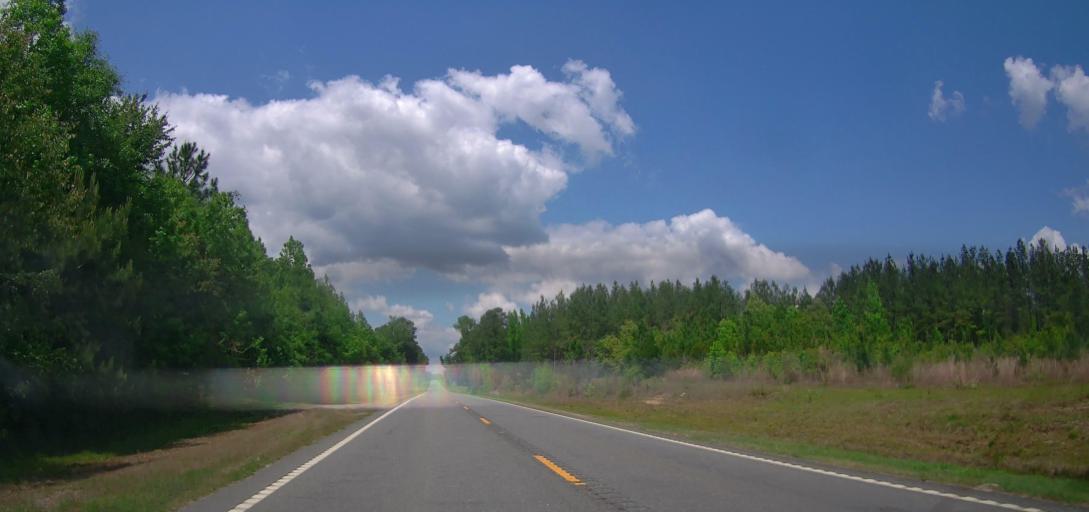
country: US
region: Georgia
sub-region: Treutlen County
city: Soperton
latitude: 32.3936
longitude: -82.6011
